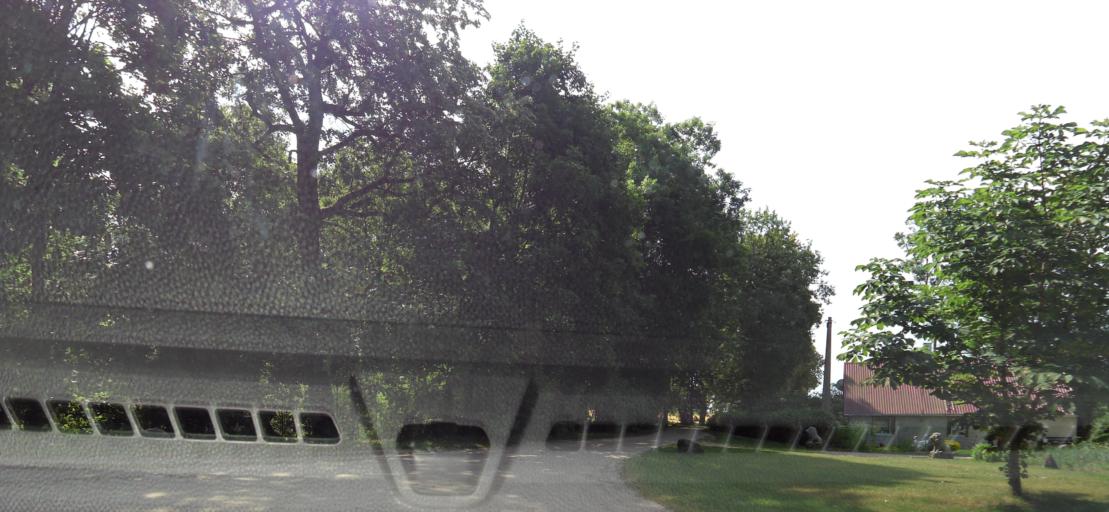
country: LT
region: Panevezys
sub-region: Birzai
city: Birzai
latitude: 56.2149
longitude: 24.6814
